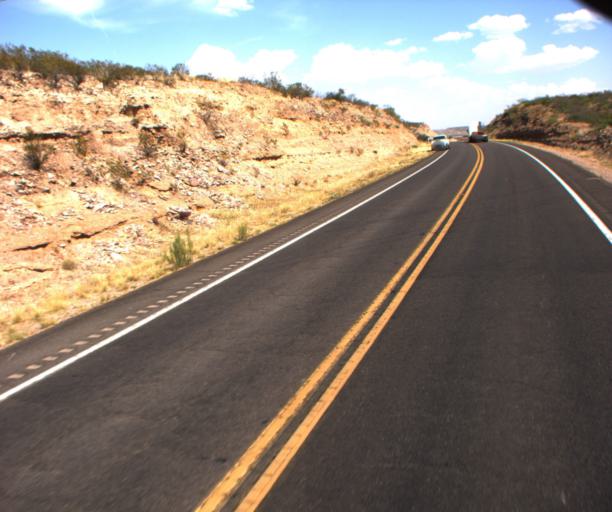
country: US
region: Arizona
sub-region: Greenlee County
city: Clifton
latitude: 32.8773
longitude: -109.1958
